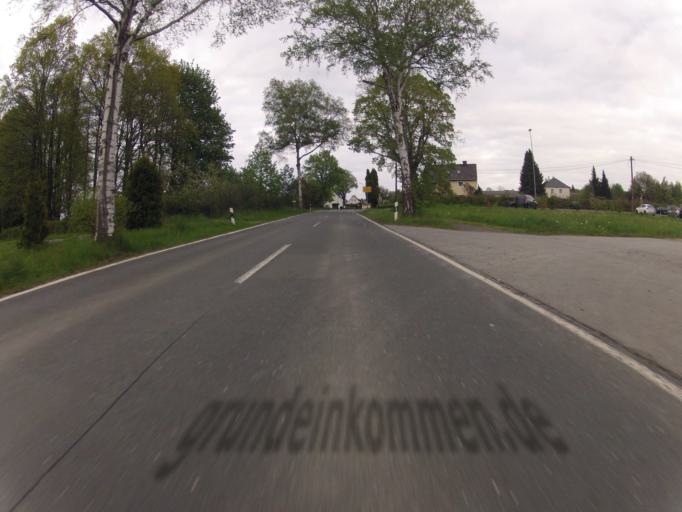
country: DE
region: Bavaria
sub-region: Upper Franconia
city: Sparneck
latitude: 50.1630
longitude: 11.8343
